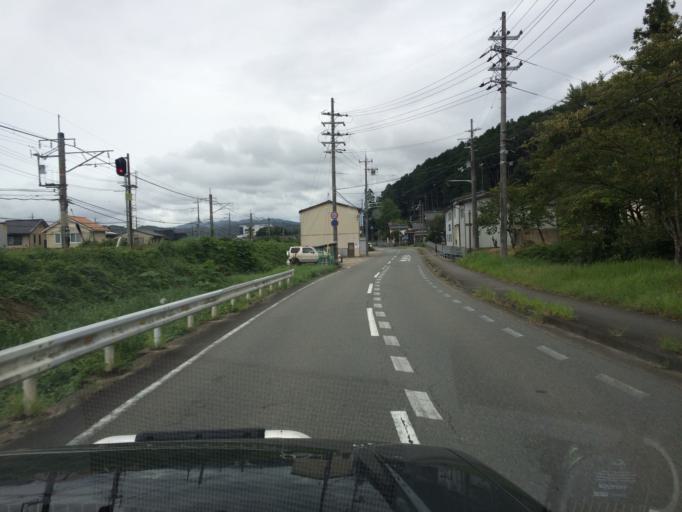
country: JP
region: Hyogo
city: Toyooka
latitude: 35.5224
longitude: 134.8188
